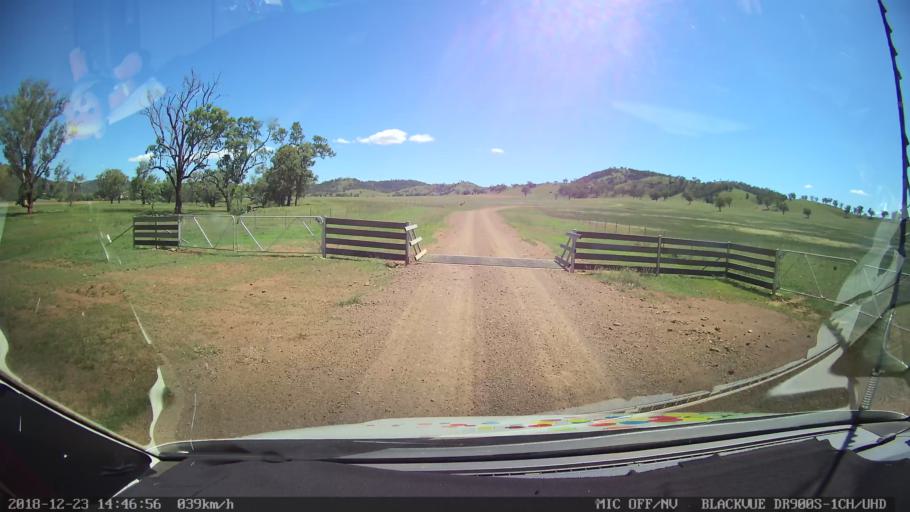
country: AU
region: New South Wales
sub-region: Tamworth Municipality
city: Manilla
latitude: -30.6495
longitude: 150.8793
